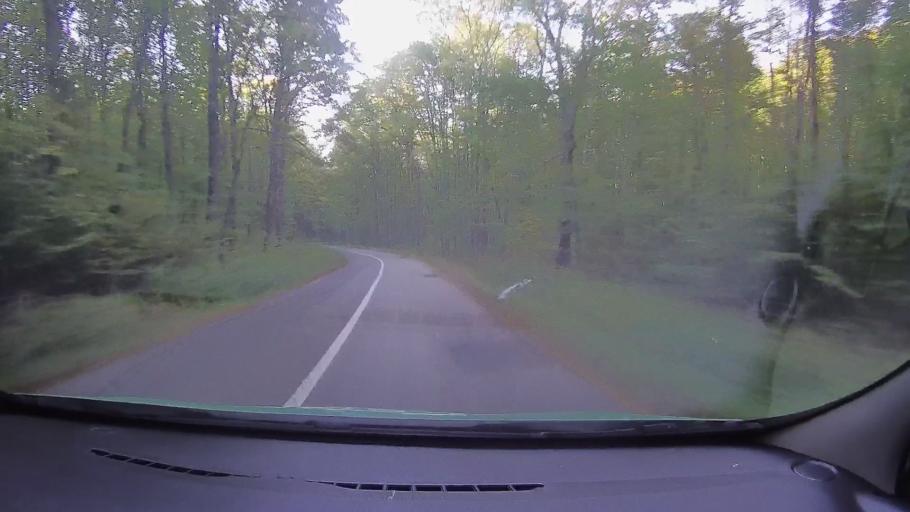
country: RO
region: Timis
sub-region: Comuna Nadrag
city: Nadrag
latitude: 45.6798
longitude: 22.1574
